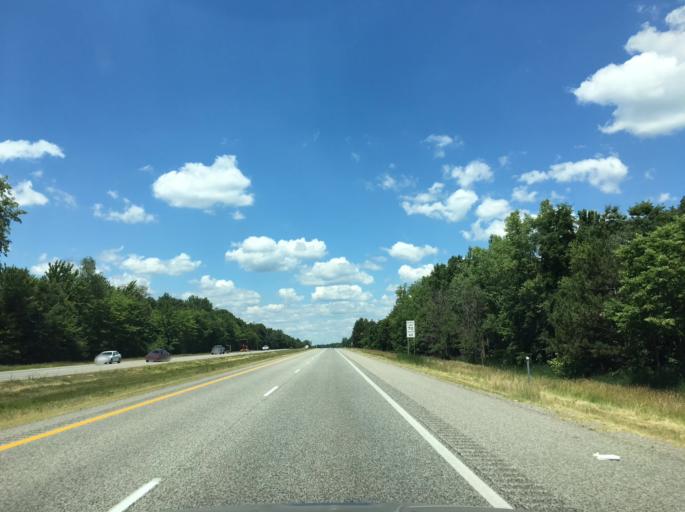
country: US
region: Michigan
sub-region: Midland County
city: Midland
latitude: 43.6479
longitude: -84.1950
